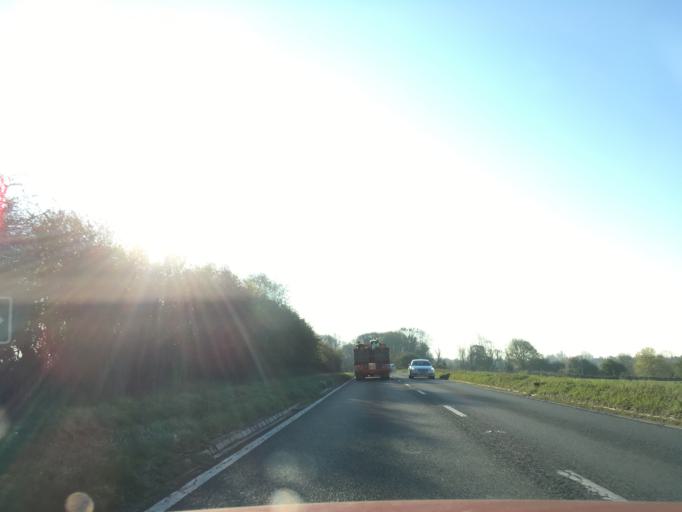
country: GB
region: England
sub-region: Oxfordshire
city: Burford
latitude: 51.8053
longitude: -1.6491
